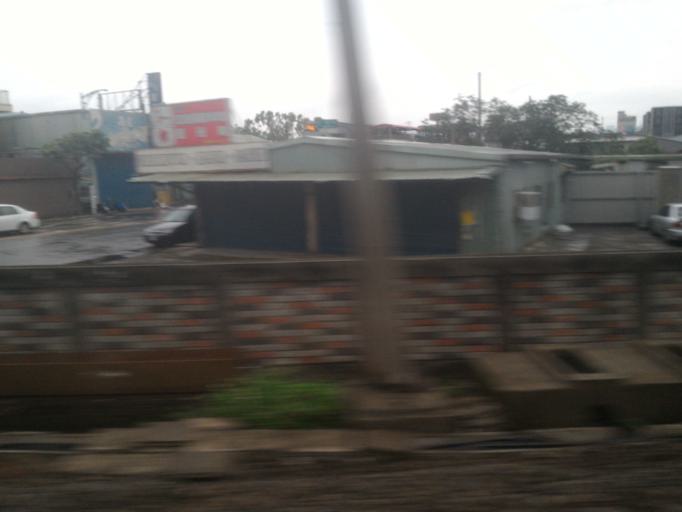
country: TW
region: Taipei
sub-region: Taipei
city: Banqiao
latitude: 25.0011
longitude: 121.4297
